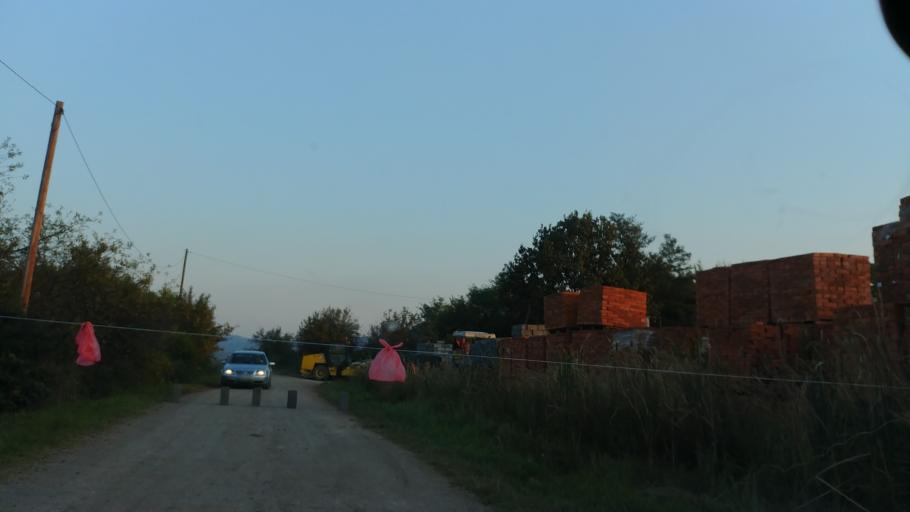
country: BA
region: Brcko
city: Brcko
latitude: 44.7688
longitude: 18.8285
